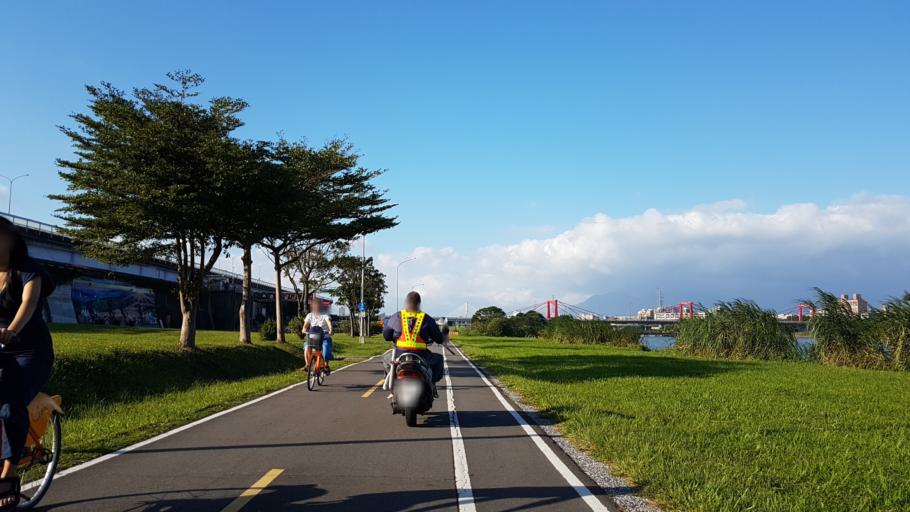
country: TW
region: Taipei
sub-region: Taipei
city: Banqiao
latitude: 25.0174
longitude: 121.4873
